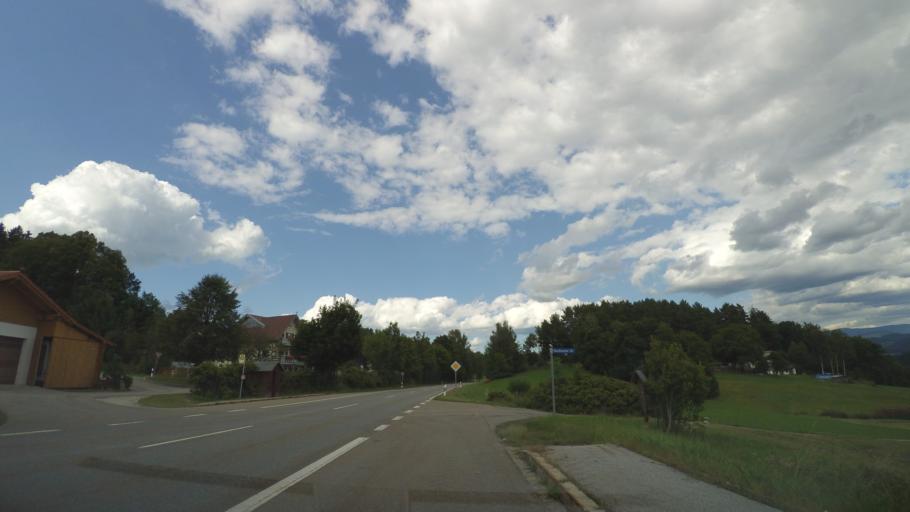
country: DE
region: Bavaria
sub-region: Lower Bavaria
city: Kollnburg
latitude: 49.0482
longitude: 12.8669
